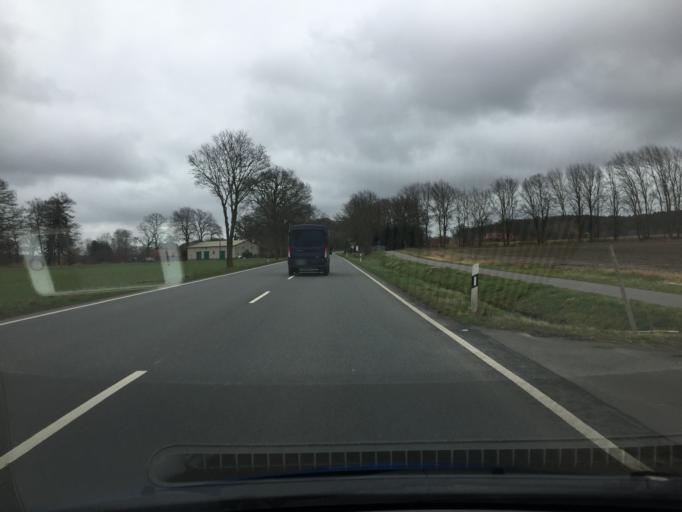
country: DE
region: Lower Saxony
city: Zernien
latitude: 53.0640
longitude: 10.8591
